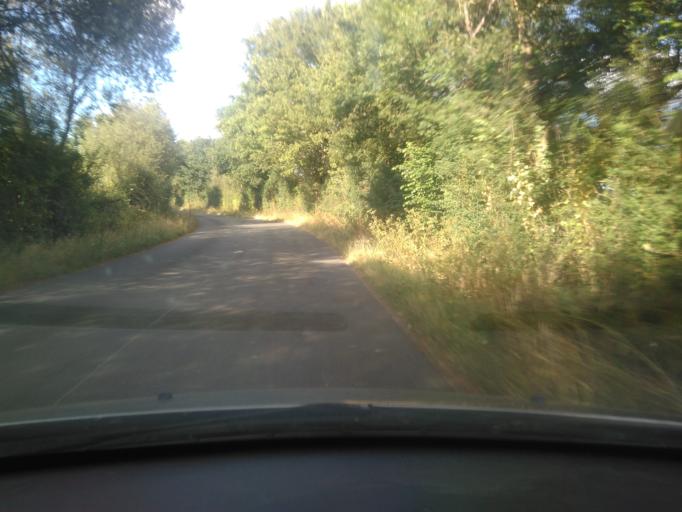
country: FR
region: Pays de la Loire
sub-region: Departement de la Vendee
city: Saint-Florent-des-Bois
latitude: 46.5793
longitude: -1.3240
